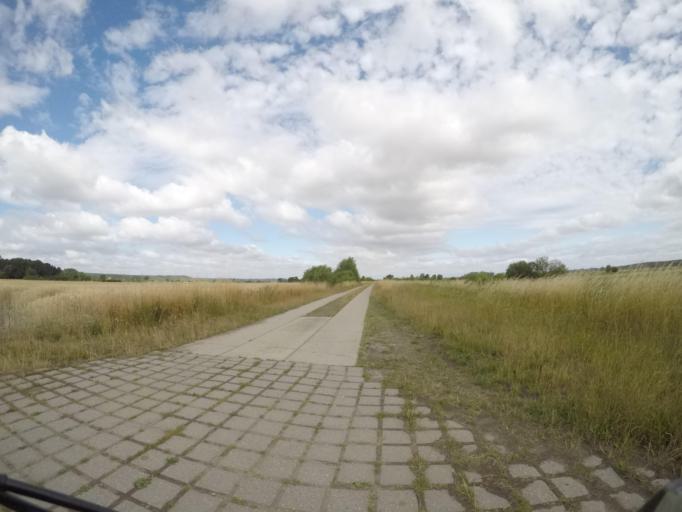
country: DE
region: Lower Saxony
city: Hitzacker
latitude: 53.1734
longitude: 11.0501
